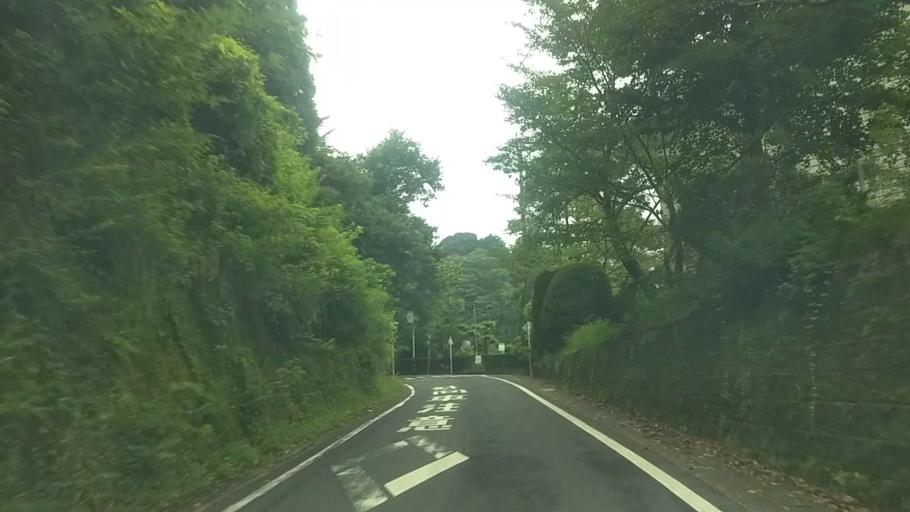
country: JP
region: Chiba
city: Kawaguchi
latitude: 35.2533
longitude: 140.0608
